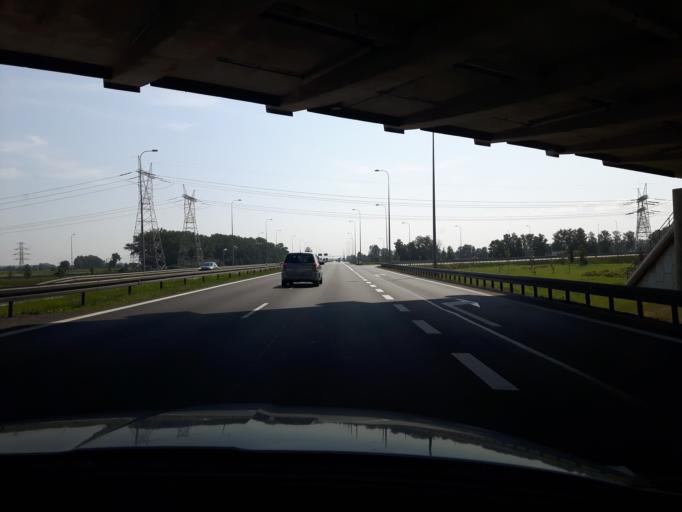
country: PL
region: Pomeranian Voivodeship
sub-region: Gdansk
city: Gdansk
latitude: 54.3168
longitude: 18.7477
